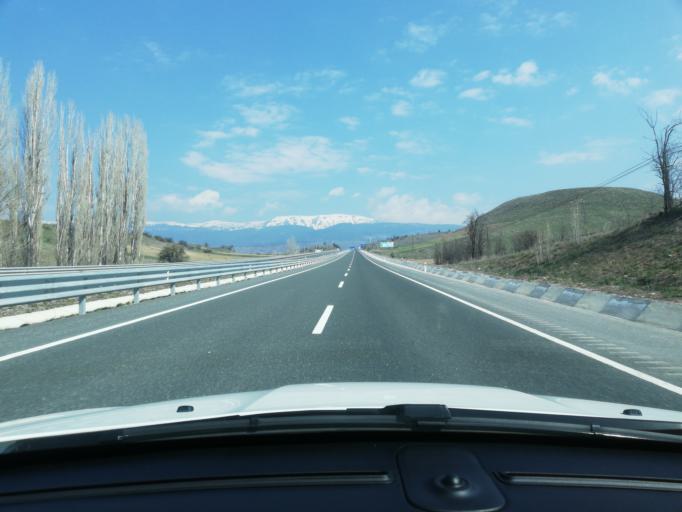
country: TR
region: Cankiri
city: Ilgaz
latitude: 40.9115
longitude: 33.6492
